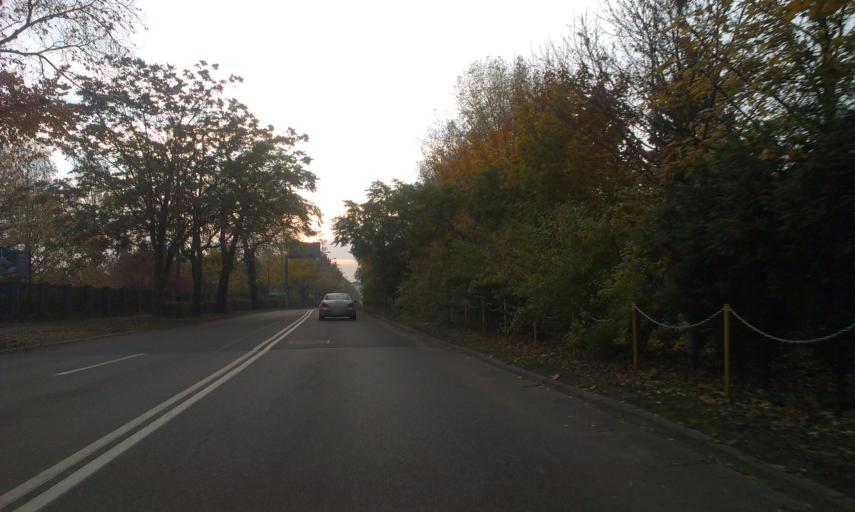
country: PL
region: Greater Poland Voivodeship
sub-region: Powiat poznanski
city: Suchy Las
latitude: 52.4205
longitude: 16.8746
